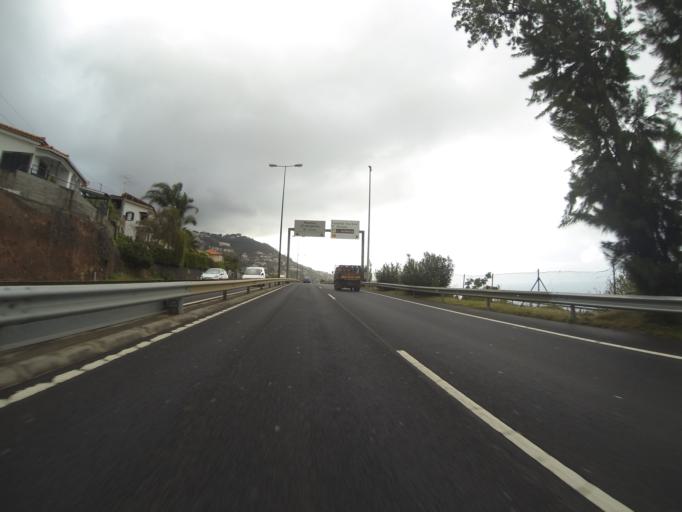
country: PT
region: Madeira
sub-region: Funchal
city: Nossa Senhora do Monte
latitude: 32.6580
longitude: -16.8874
